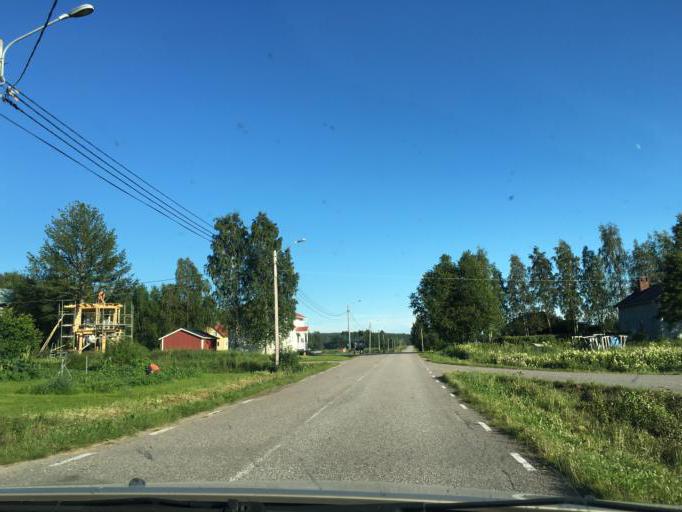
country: SE
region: Norrbotten
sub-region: Kalix Kommun
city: Rolfs
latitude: 65.8994
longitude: 22.9360
